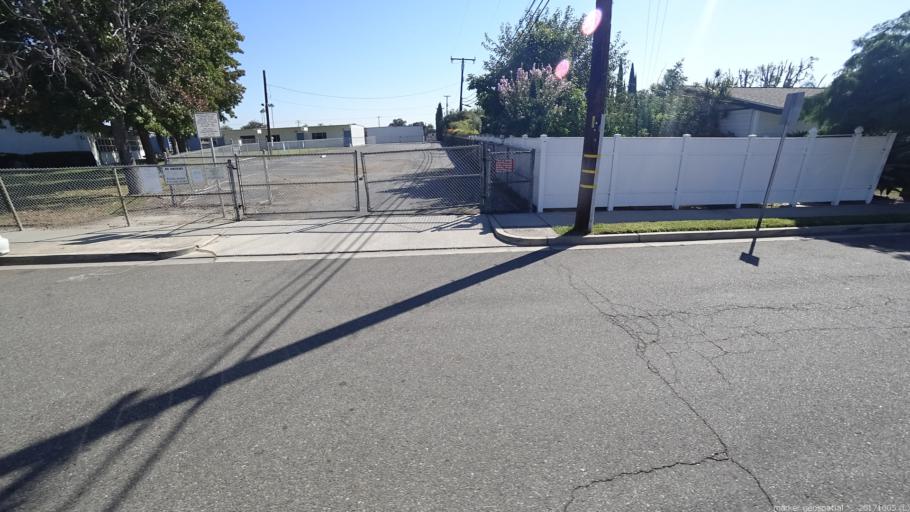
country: US
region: California
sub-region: Orange County
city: Stanton
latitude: 33.7985
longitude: -117.9775
